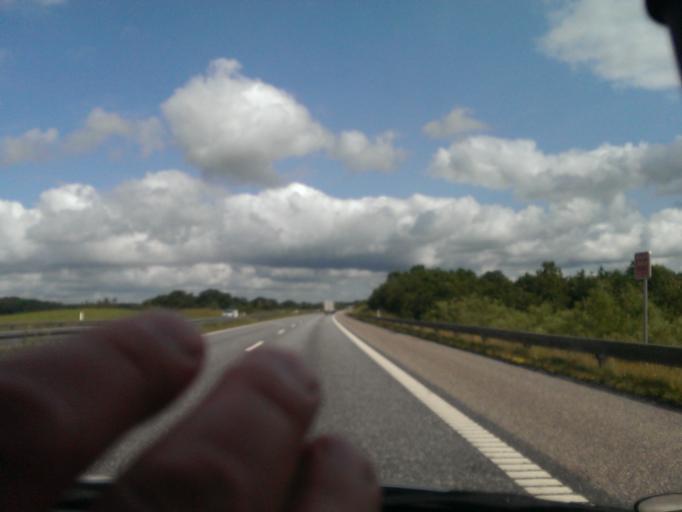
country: DK
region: North Denmark
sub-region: Mariagerfjord Kommune
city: Hobro
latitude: 56.6932
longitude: 9.7292
